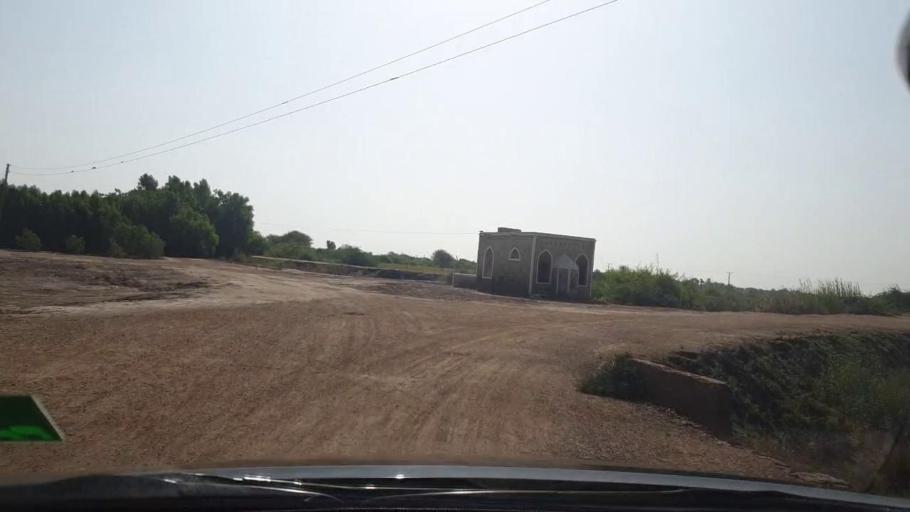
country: PK
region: Sindh
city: Tando Bago
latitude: 24.6972
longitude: 69.0180
